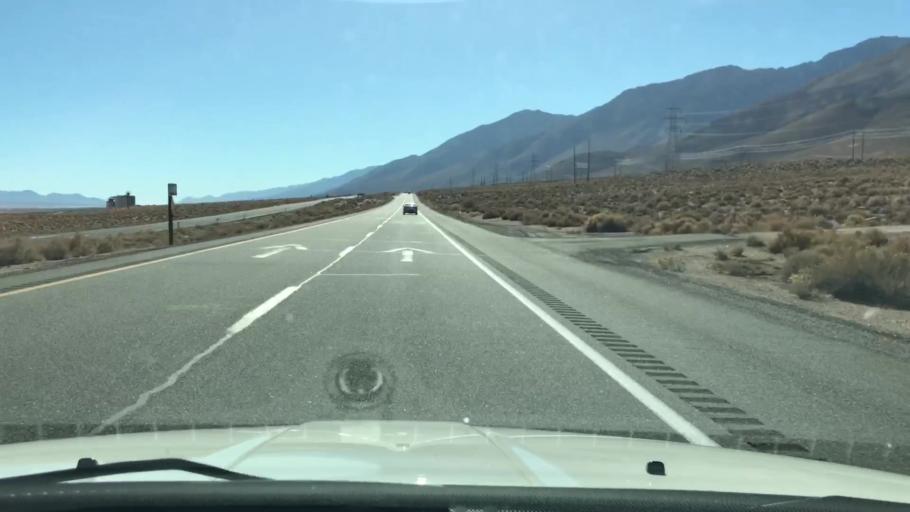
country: US
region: California
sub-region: Inyo County
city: Lone Pine
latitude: 36.4873
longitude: -118.0346
